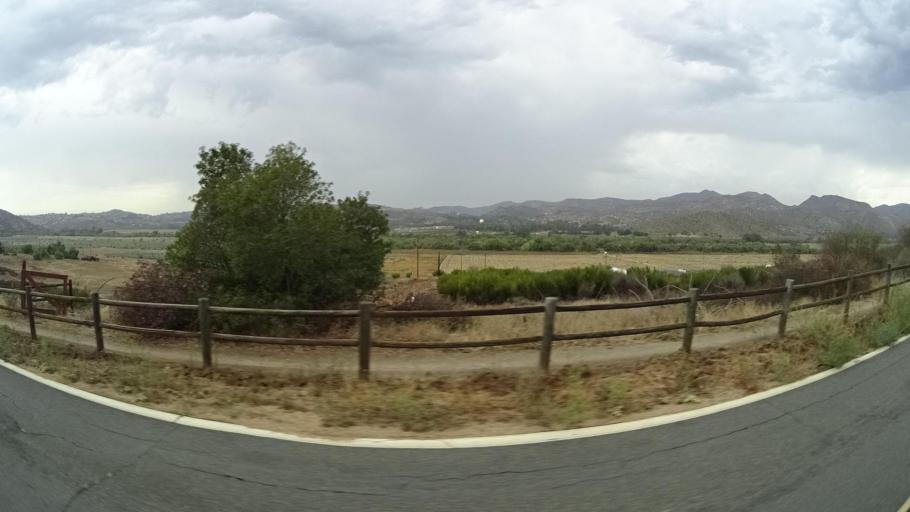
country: US
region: California
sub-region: San Diego County
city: San Pasqual
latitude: 33.0758
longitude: -116.9940
